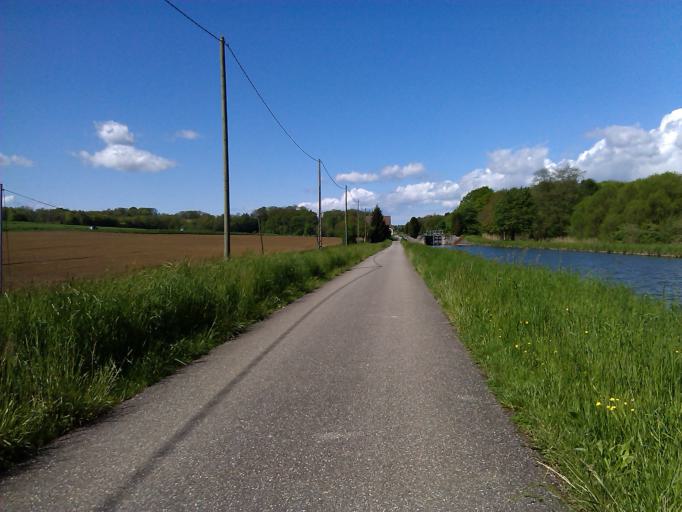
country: FR
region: Alsace
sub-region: Departement du Haut-Rhin
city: Dannemarie
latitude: 47.6347
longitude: 7.0785
